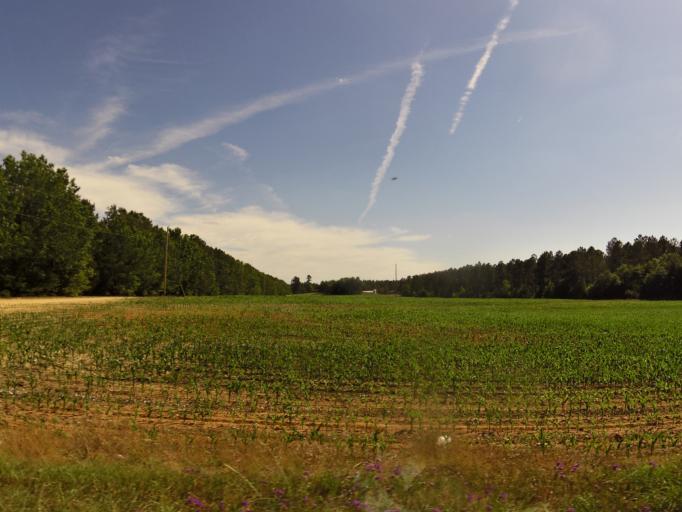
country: US
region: South Carolina
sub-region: Bamberg County
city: Denmark
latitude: 33.3391
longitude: -81.1746
